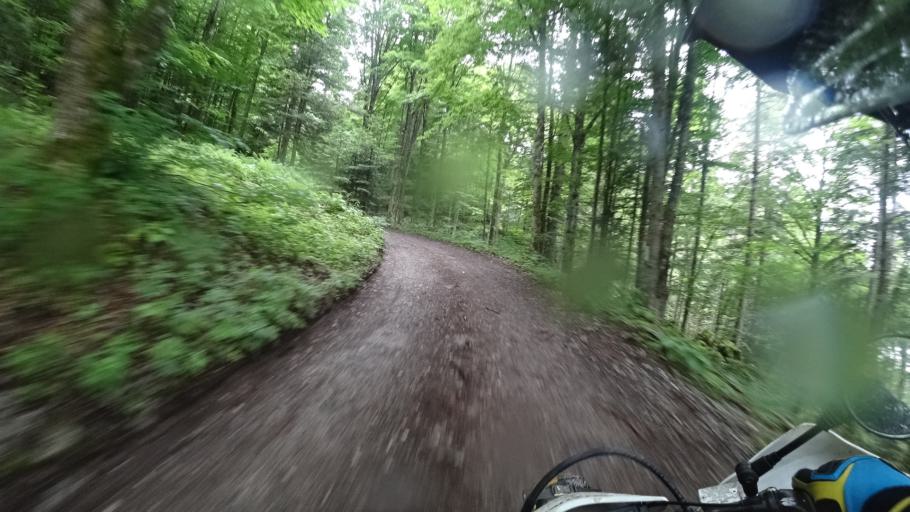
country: HR
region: Primorsko-Goranska
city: Vrbovsko
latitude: 45.2977
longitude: 14.9420
